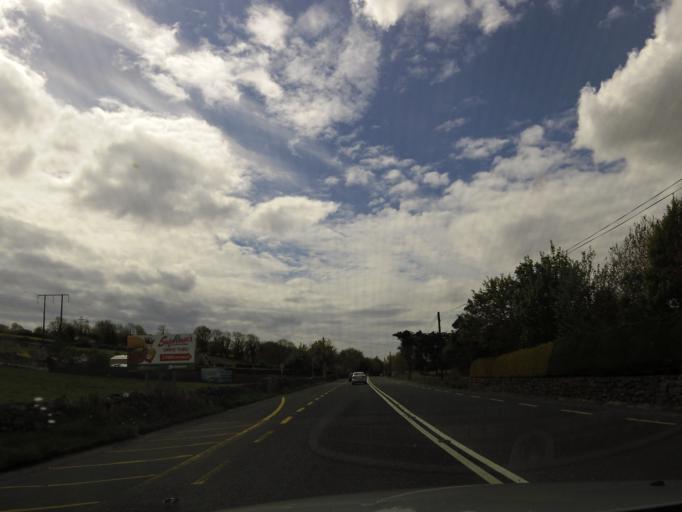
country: IE
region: Connaught
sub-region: County Galway
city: Claregalway
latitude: 53.3086
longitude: -8.9925
